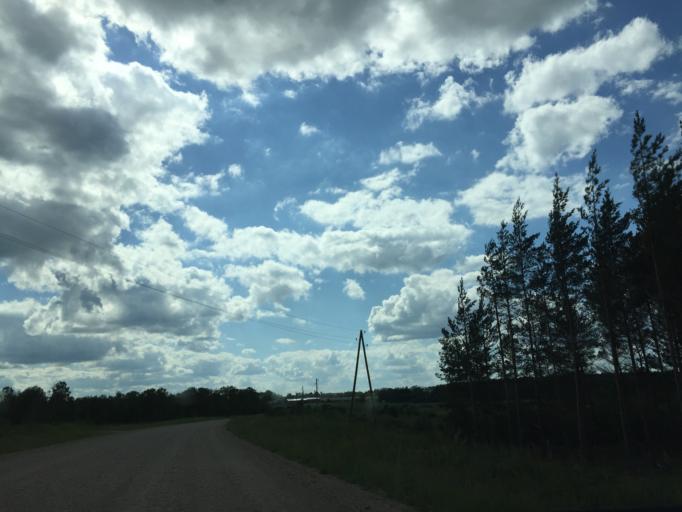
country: LV
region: Tukuma Rajons
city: Tukums
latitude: 56.9094
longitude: 23.1673
